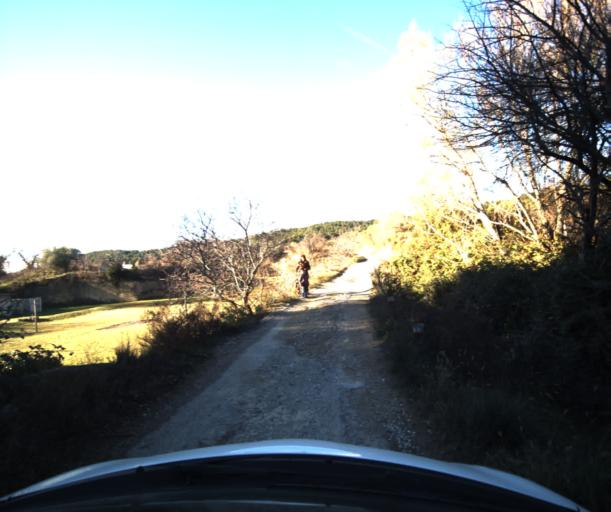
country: FR
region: Provence-Alpes-Cote d'Azur
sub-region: Departement du Vaucluse
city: Pertuis
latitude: 43.7051
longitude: 5.4843
